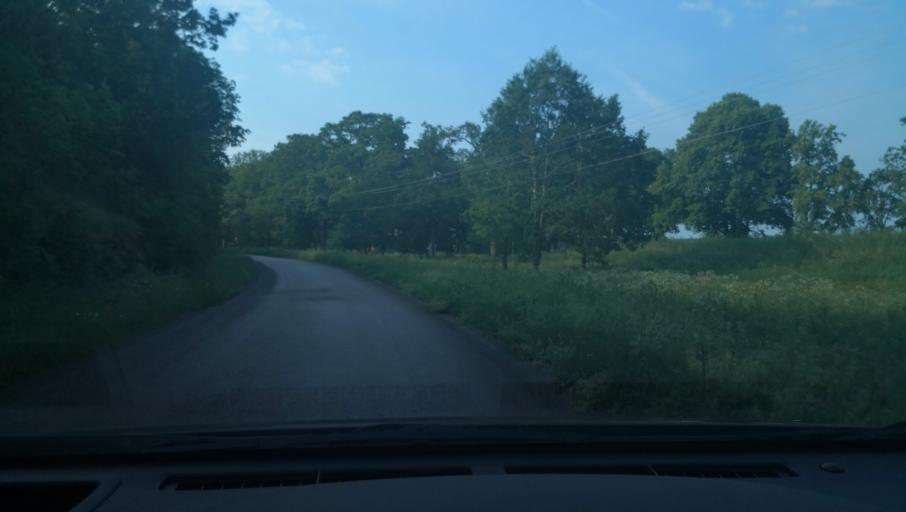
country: SE
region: Vaestmanland
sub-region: Arboga Kommun
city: Tyringe
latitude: 59.3976
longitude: 15.9322
